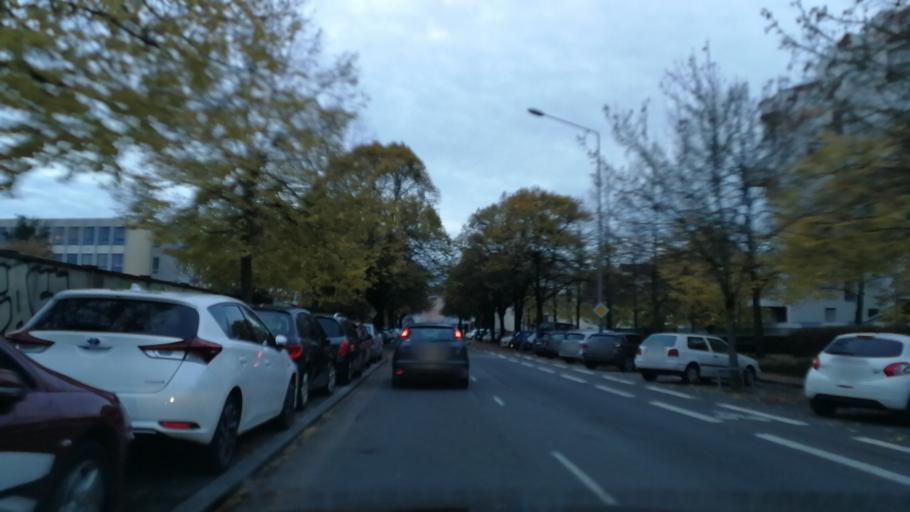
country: FR
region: Bourgogne
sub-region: Departement de la Cote-d'Or
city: Saint-Apollinaire
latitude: 47.3263
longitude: 5.0526
